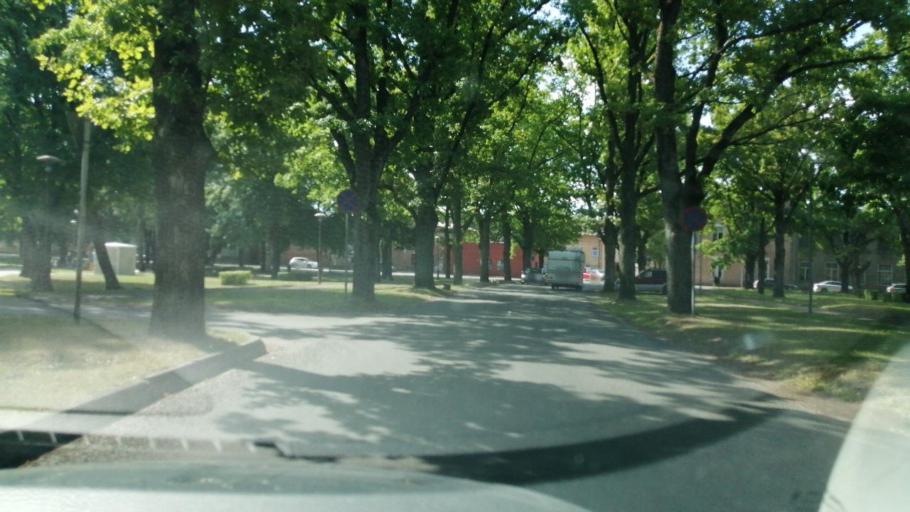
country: EE
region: Viljandimaa
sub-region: Viljandi linn
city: Viljandi
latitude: 58.3688
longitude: 25.6027
